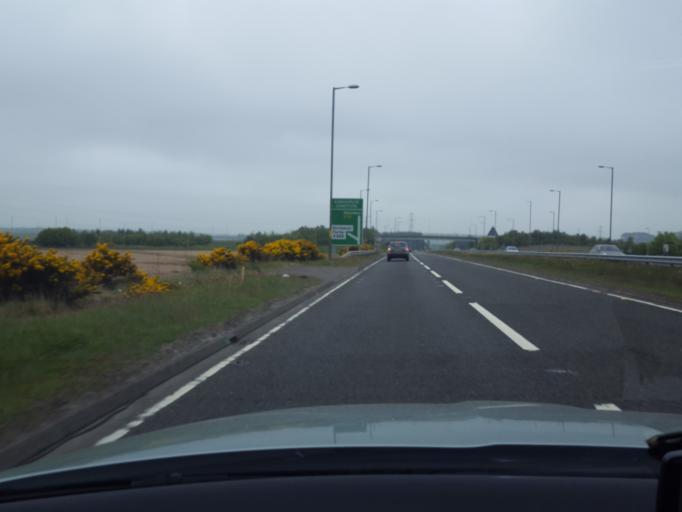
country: GB
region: Scotland
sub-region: Angus
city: Forfar
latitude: 56.6506
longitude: -2.9220
